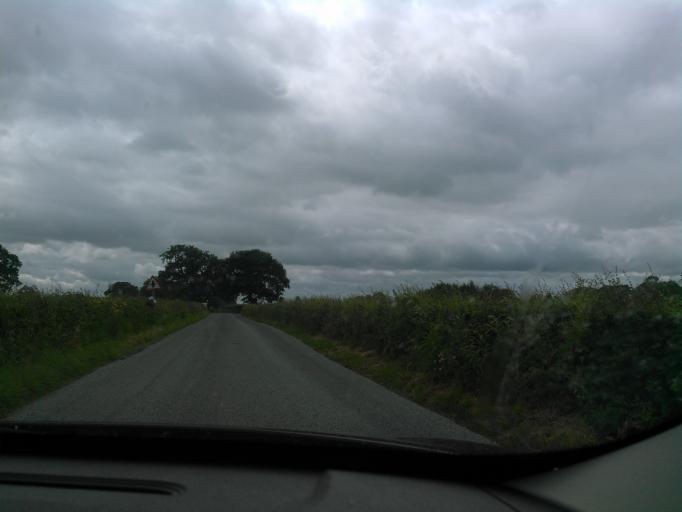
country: GB
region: England
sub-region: Shropshire
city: Wem
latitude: 52.8826
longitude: -2.7489
